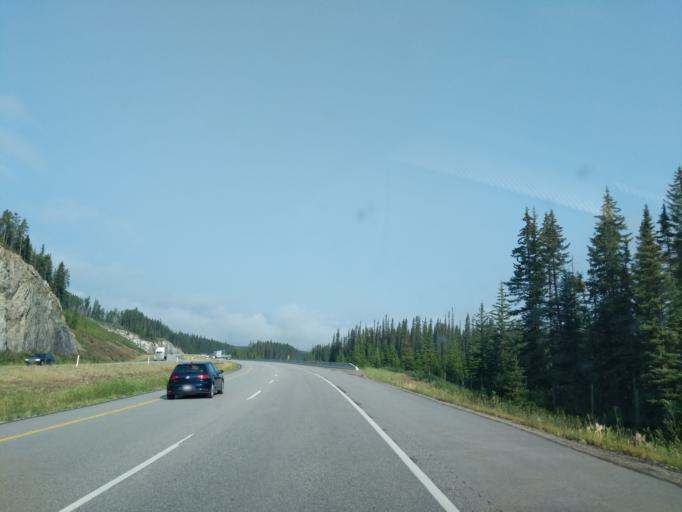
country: CA
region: Alberta
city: Banff
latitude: 51.2550
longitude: -115.8937
